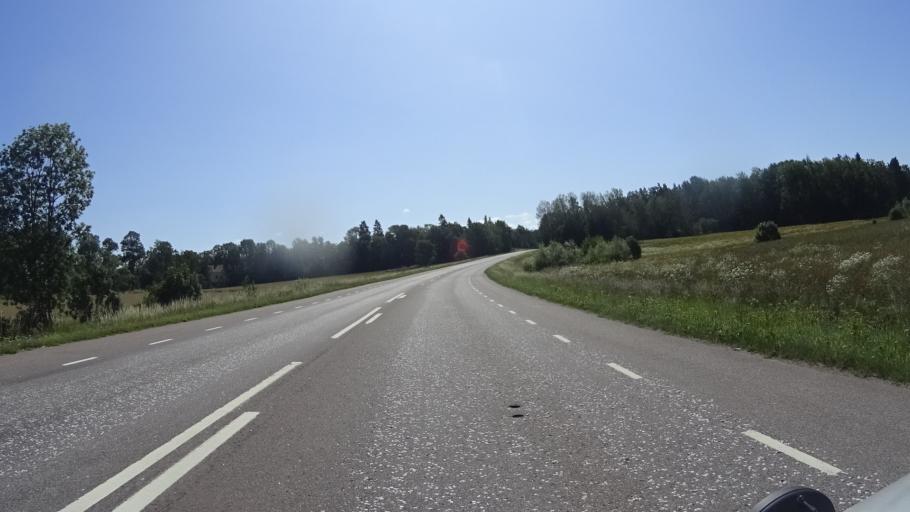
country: SE
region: OEstergoetland
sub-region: Vadstena Kommun
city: Herrestad
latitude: 58.3101
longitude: 14.9075
